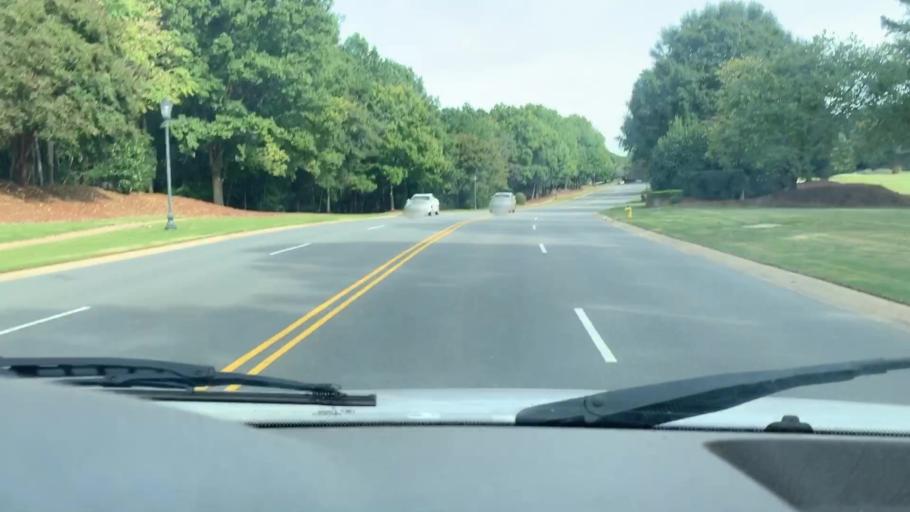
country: US
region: North Carolina
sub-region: Mecklenburg County
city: Cornelius
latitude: 35.4755
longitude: -80.9059
